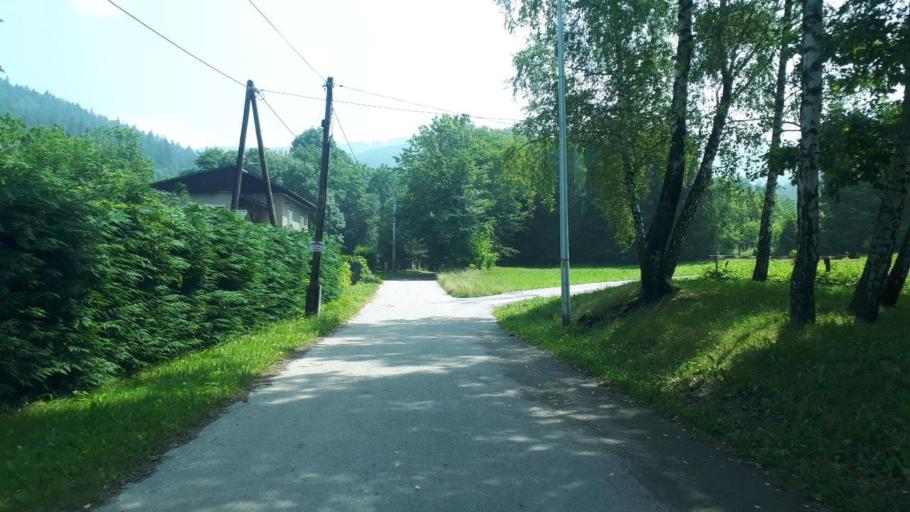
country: PL
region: Silesian Voivodeship
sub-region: Powiat cieszynski
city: Ustron
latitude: 49.7256
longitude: 18.8270
